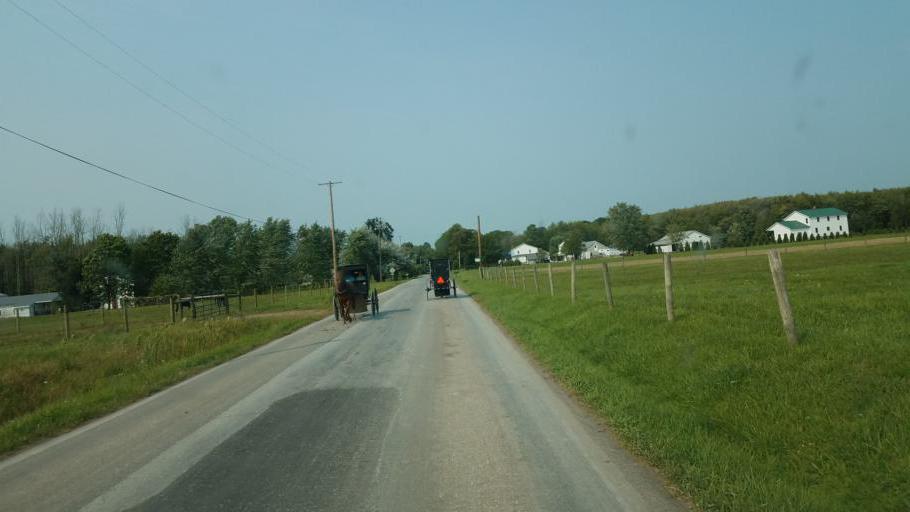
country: US
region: Ohio
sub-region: Geauga County
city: Middlefield
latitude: 41.4955
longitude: -81.0031
